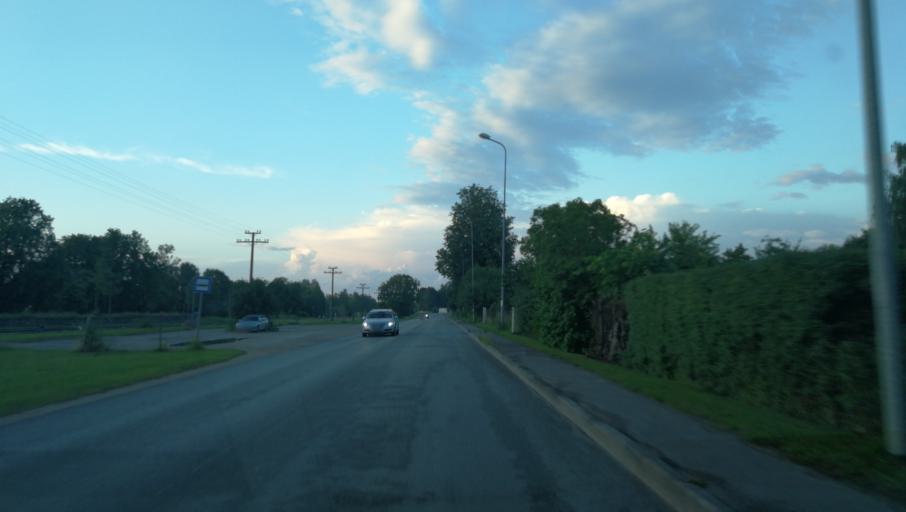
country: LV
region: Cesu Rajons
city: Cesis
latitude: 57.3181
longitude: 25.2888
